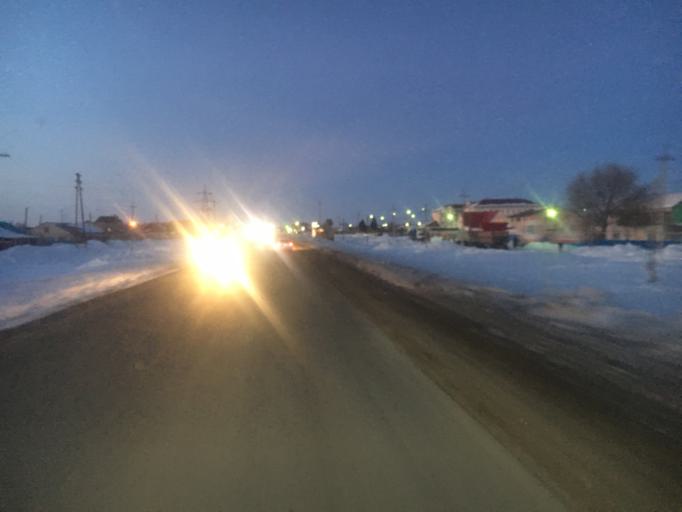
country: KZ
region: Batys Qazaqstan
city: Oral
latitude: 51.1456
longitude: 51.4879
